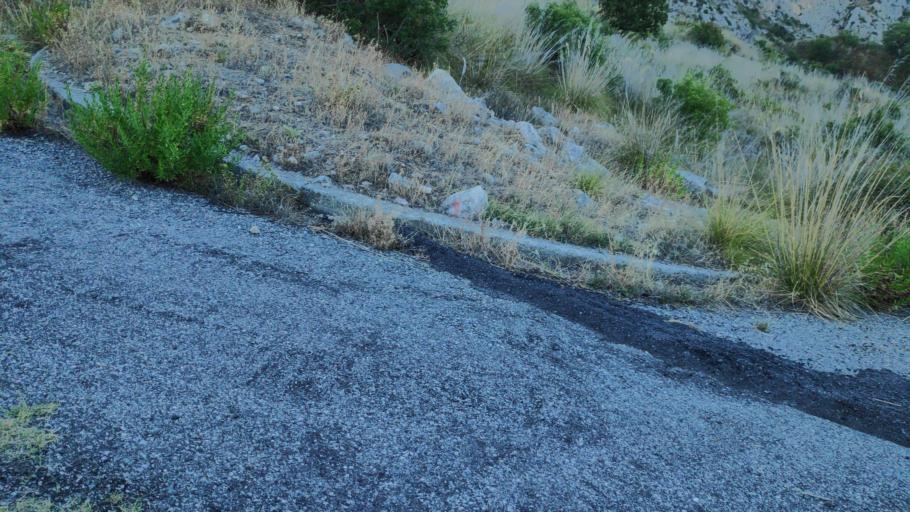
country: IT
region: Calabria
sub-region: Provincia di Reggio Calabria
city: Pazzano
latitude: 38.4634
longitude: 16.4477
